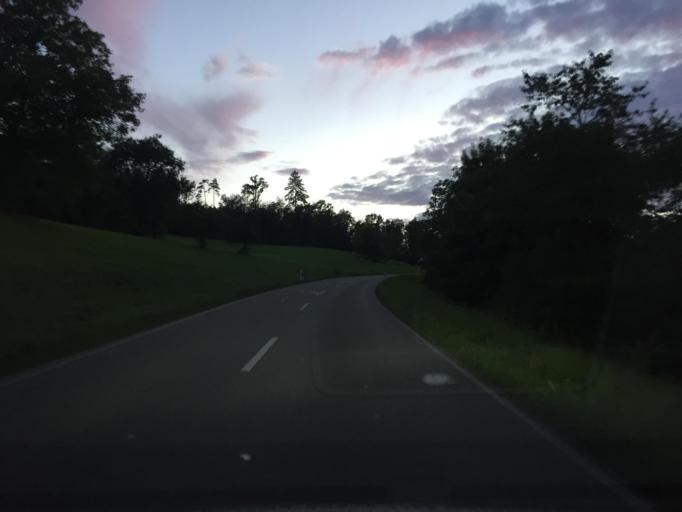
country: DE
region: Baden-Wuerttemberg
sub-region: Freiburg Region
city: Eggingen
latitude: 47.6630
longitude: 8.4170
